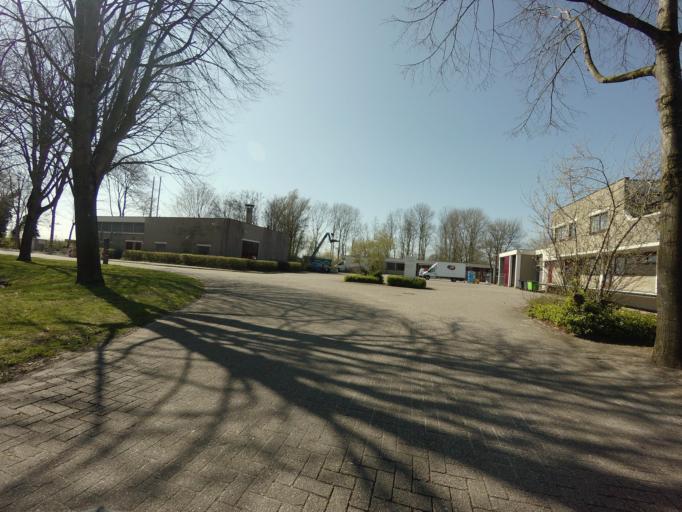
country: NL
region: South Holland
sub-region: Bodegraven-Reeuwijk
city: Bodegraven
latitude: 52.1050
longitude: 4.7184
